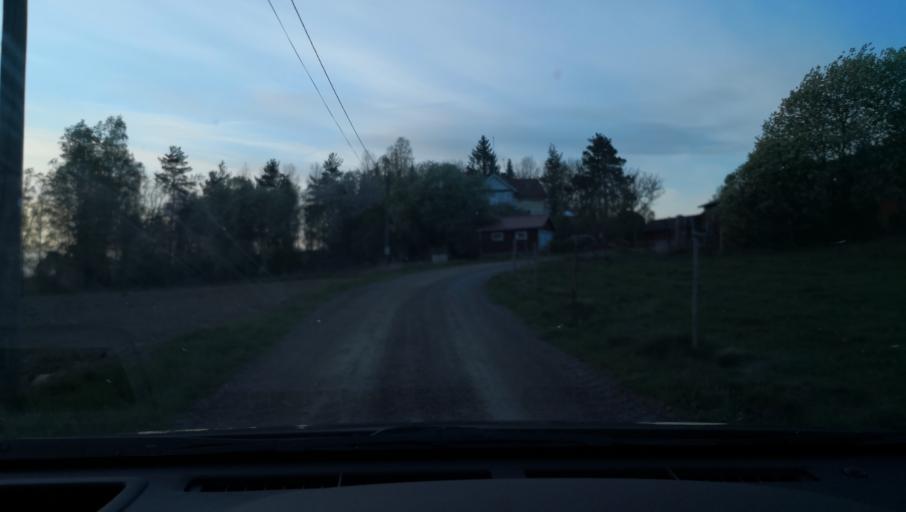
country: SE
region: OErebro
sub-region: Askersunds Kommun
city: Askersund
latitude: 58.9664
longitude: 14.9502
